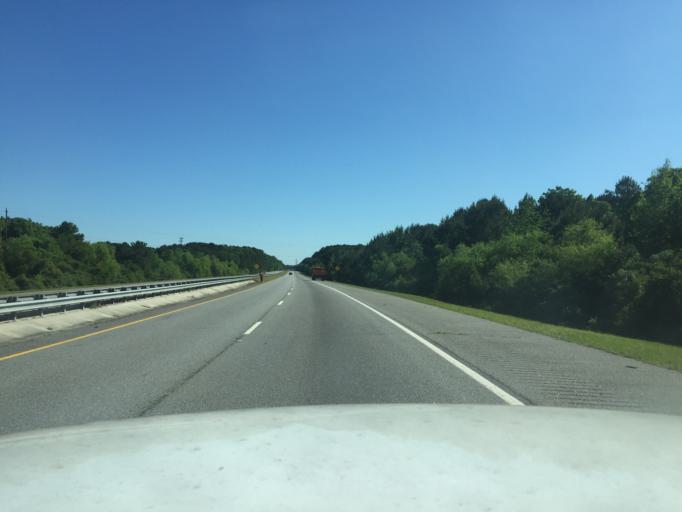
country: US
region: Georgia
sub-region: Chatham County
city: Georgetown
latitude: 32.0174
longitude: -81.1744
